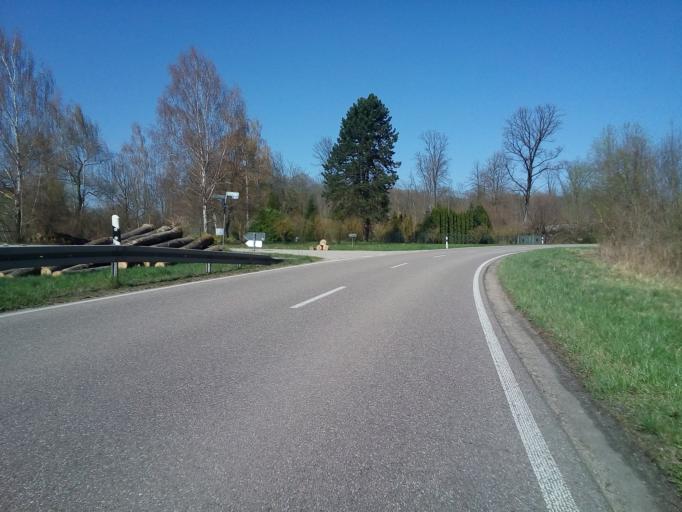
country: DE
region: Baden-Wuerttemberg
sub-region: Freiburg Region
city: Rheinau
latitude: 48.6746
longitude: 7.9134
